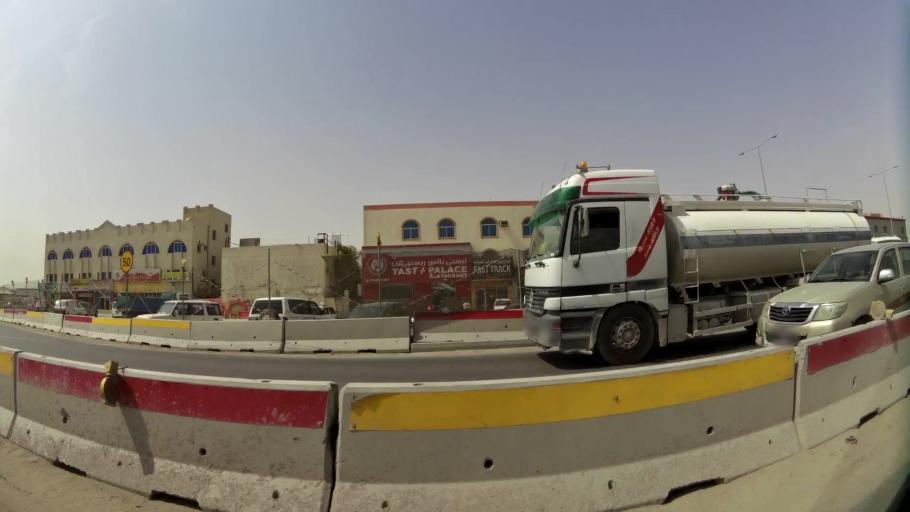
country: QA
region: Baladiyat ar Rayyan
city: Ar Rayyan
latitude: 25.2010
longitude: 51.4280
